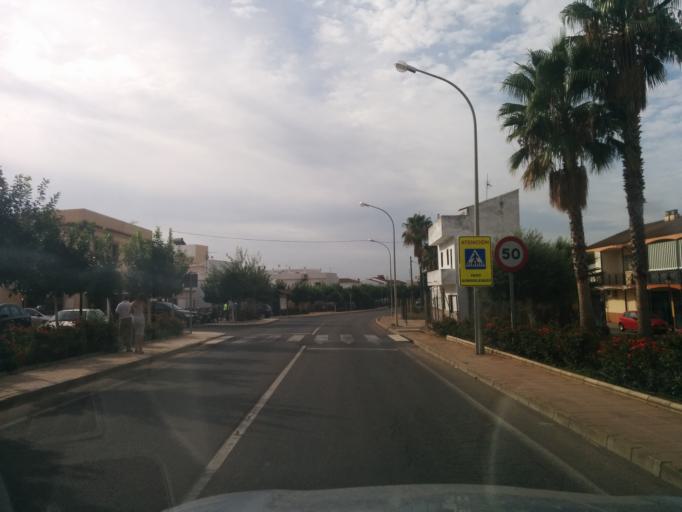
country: ES
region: Andalusia
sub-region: Provincia de Sevilla
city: Guillena
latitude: 37.5148
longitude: -6.0274
